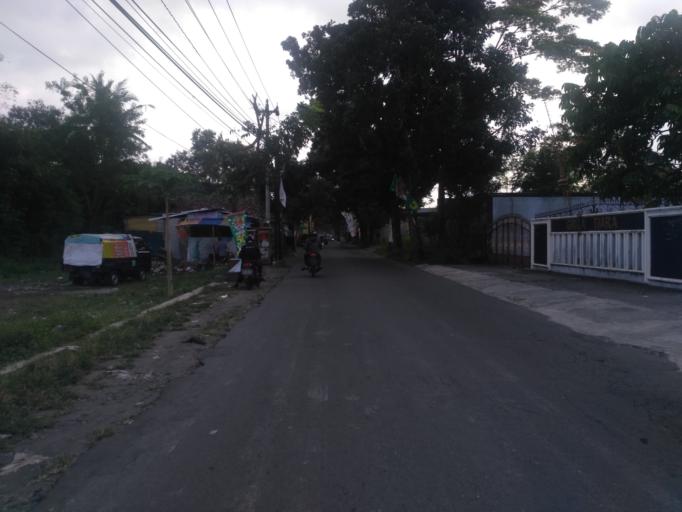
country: ID
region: Daerah Istimewa Yogyakarta
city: Yogyakarta
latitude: -7.7692
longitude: 110.3435
